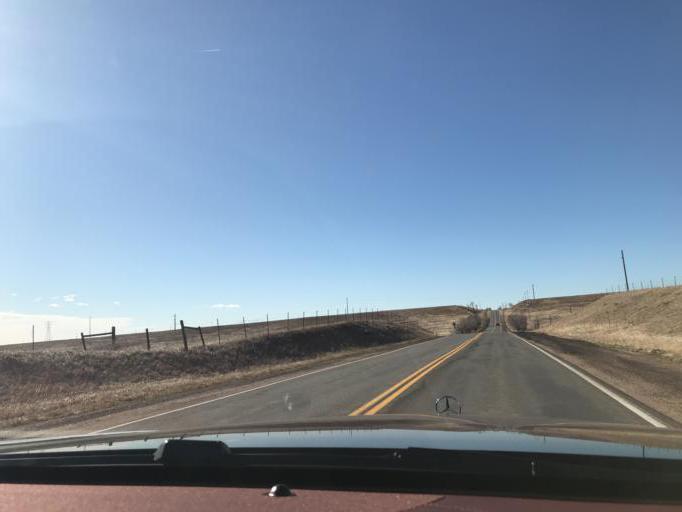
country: US
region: Colorado
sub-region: Boulder County
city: Superior
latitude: 39.8978
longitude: -105.1656
